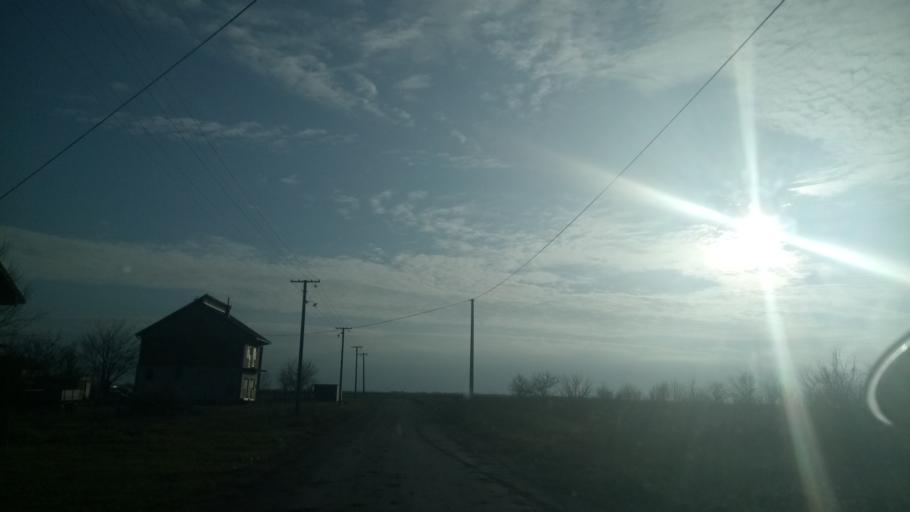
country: RS
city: Vojka
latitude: 44.9368
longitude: 20.1292
